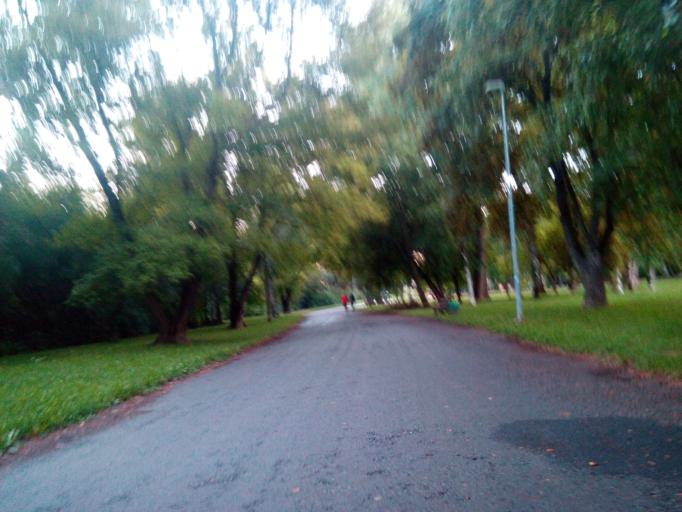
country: SK
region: Kosicky
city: Kosice
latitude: 48.7492
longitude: 21.2530
